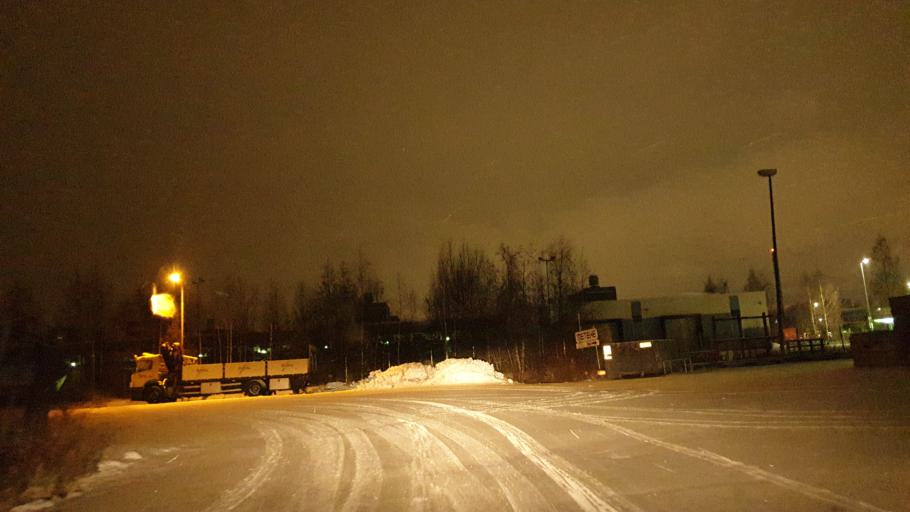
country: FI
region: Northern Ostrobothnia
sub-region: Oulu
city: Oulu
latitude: 64.9930
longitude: 25.4541
